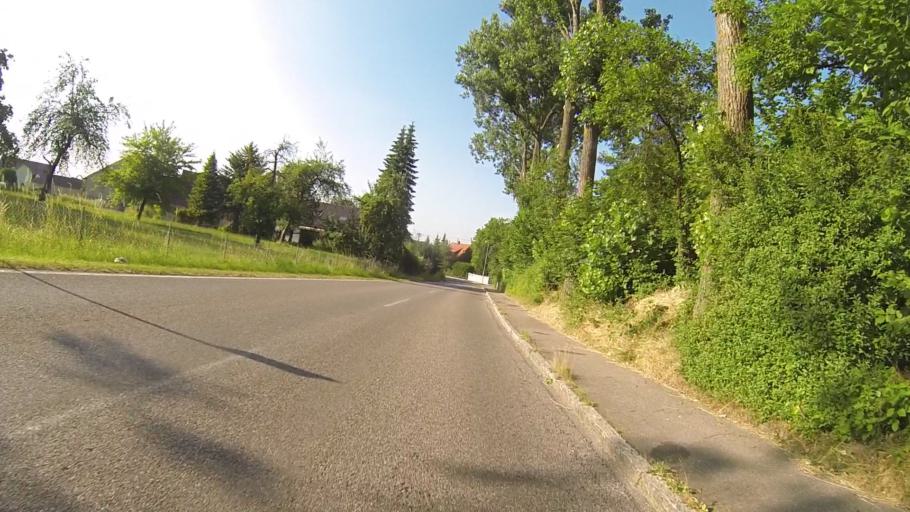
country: DE
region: Baden-Wuerttemberg
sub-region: Tuebingen Region
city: Staig
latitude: 48.3274
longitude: 9.9695
